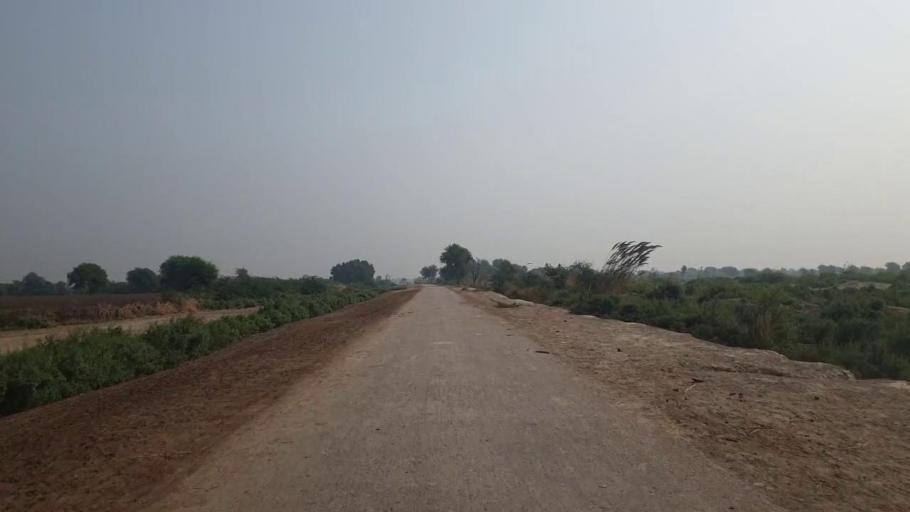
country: PK
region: Sindh
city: Tando Muhammad Khan
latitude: 25.2703
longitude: 68.4934
